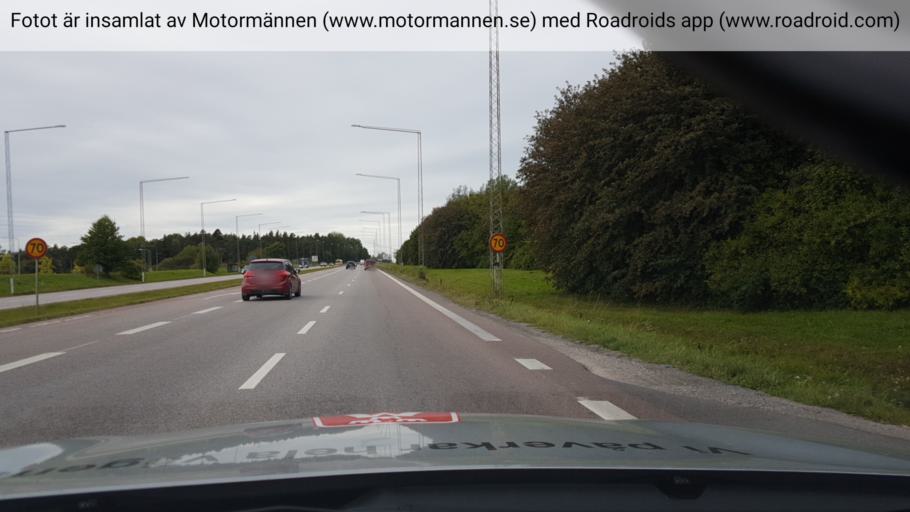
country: SE
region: Uppsala
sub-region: Uppsala Kommun
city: Uppsala
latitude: 59.8523
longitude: 17.5844
